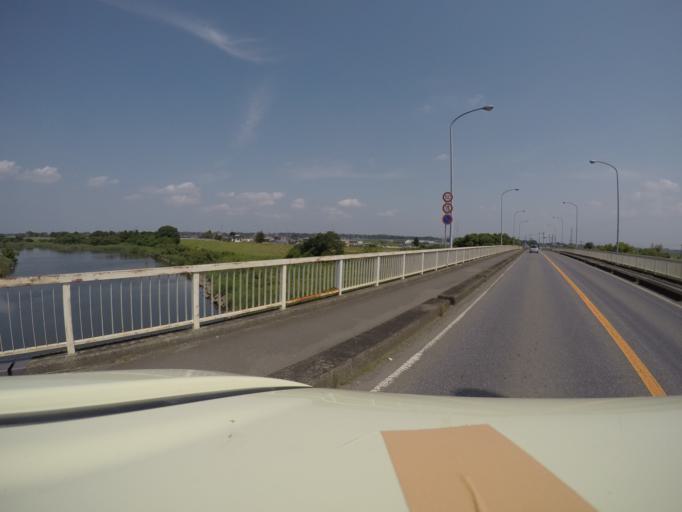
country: JP
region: Ibaraki
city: Mitsukaido
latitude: 36.0197
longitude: 140.0057
